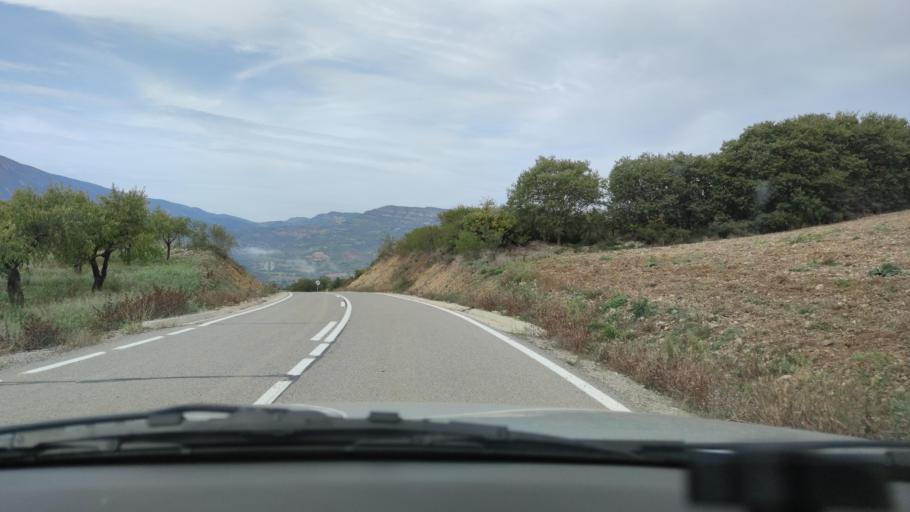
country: ES
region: Catalonia
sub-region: Provincia de Lleida
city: Llimiana
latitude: 42.0658
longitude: 0.9165
